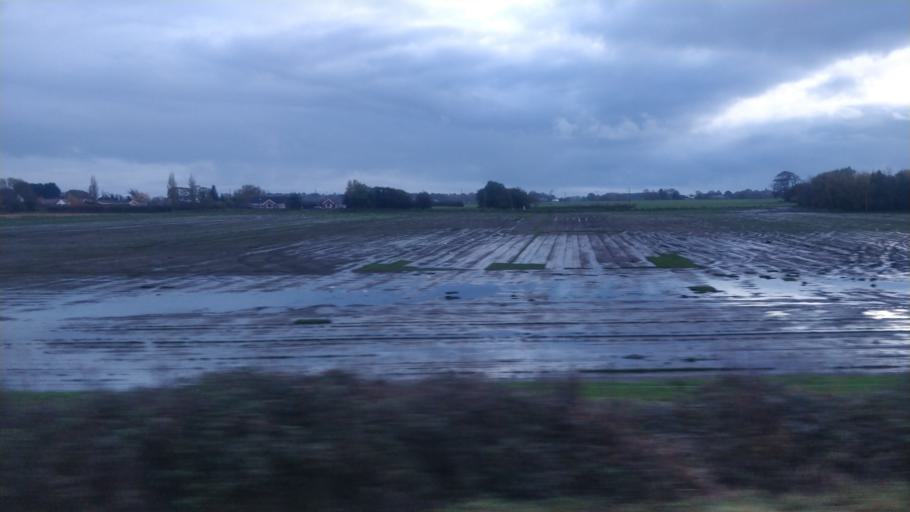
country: GB
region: England
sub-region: Lancashire
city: Ormskirk
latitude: 53.6215
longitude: -2.9050
